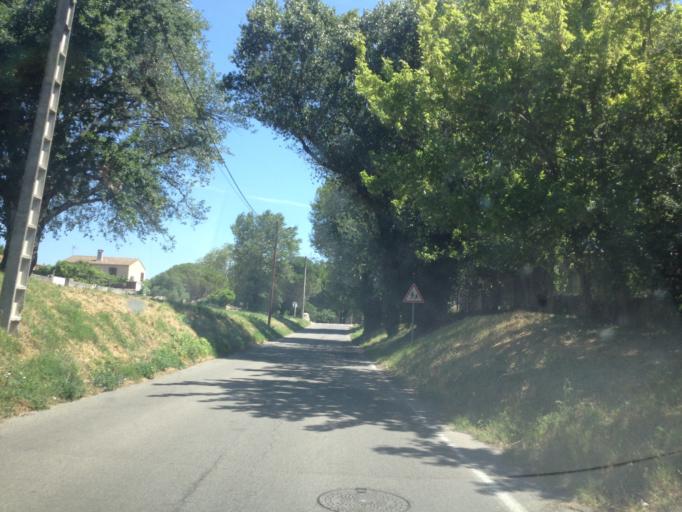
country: FR
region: Provence-Alpes-Cote d'Azur
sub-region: Departement du Vaucluse
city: Sorgues
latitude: 44.0173
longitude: 4.8758
